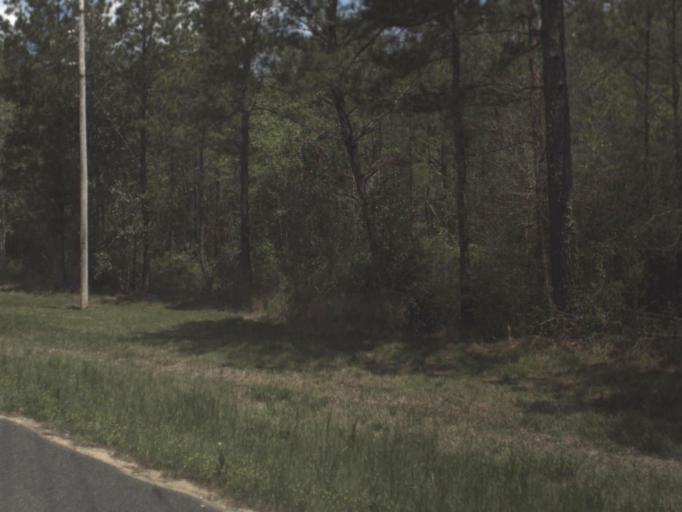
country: US
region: Florida
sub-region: Okaloosa County
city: Crestview
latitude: 30.9425
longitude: -86.6345
